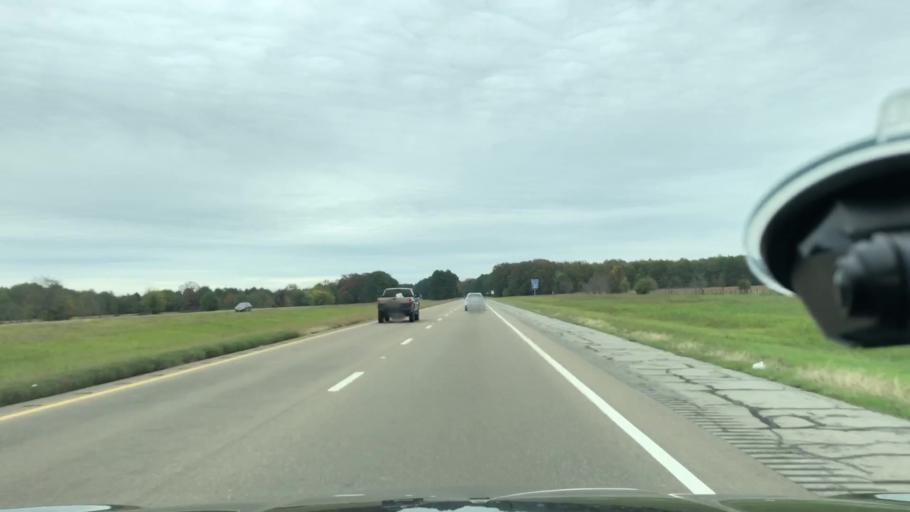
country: US
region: Texas
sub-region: Morris County
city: Naples
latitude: 33.2952
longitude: -94.7286
